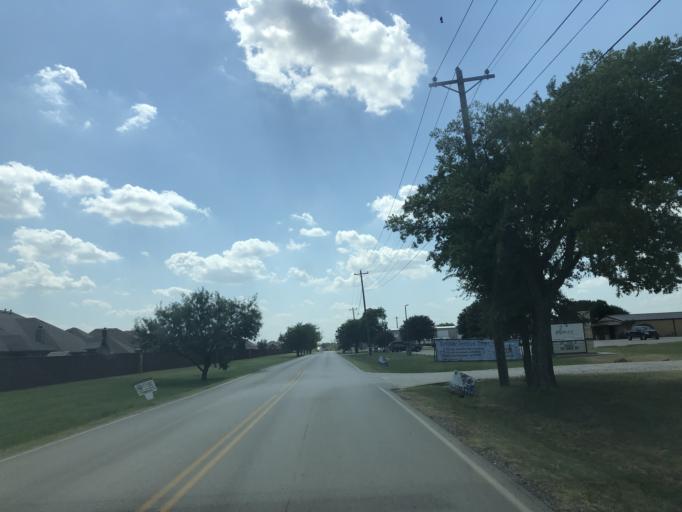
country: US
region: Texas
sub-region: Tarrant County
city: Haslet
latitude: 32.9312
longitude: -97.3253
